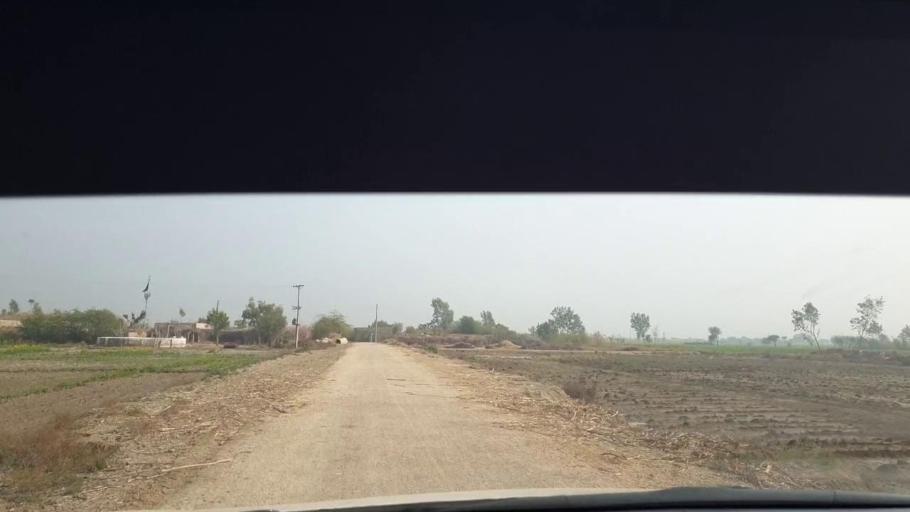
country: PK
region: Sindh
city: Berani
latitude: 25.8222
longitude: 68.8408
